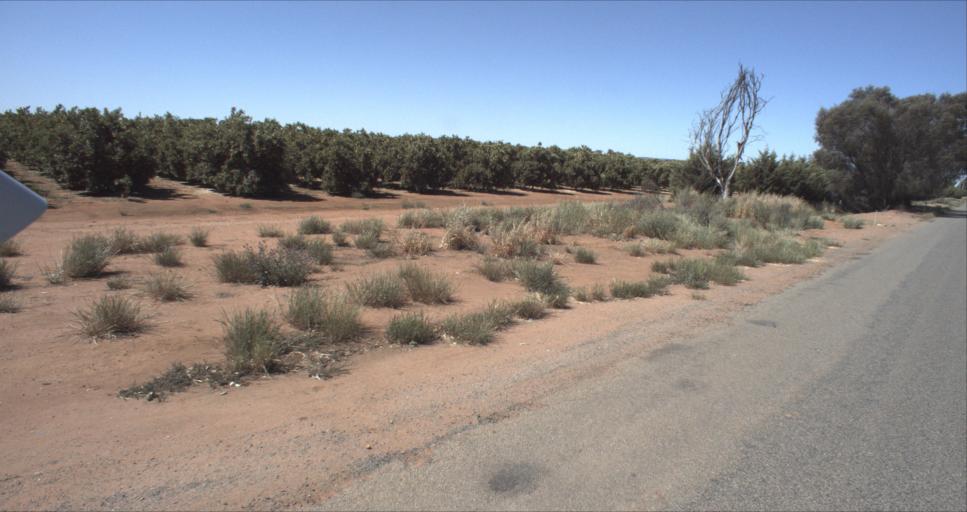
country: AU
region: New South Wales
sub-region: Leeton
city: Leeton
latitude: -34.5329
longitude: 146.3477
